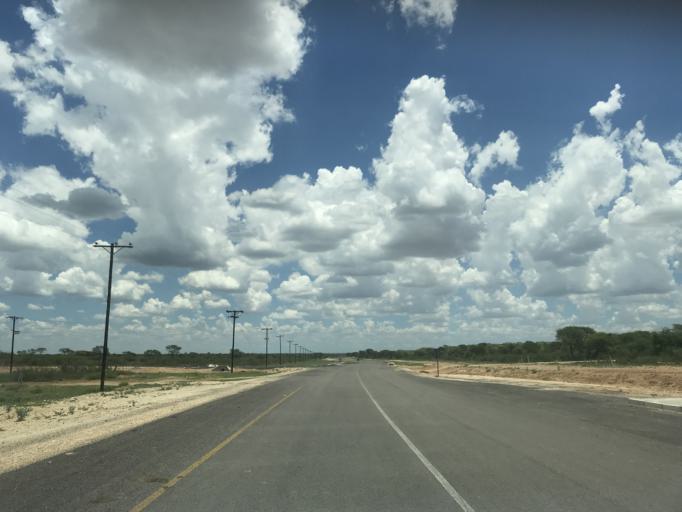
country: BW
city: Mabuli
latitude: -25.7883
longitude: 24.9012
